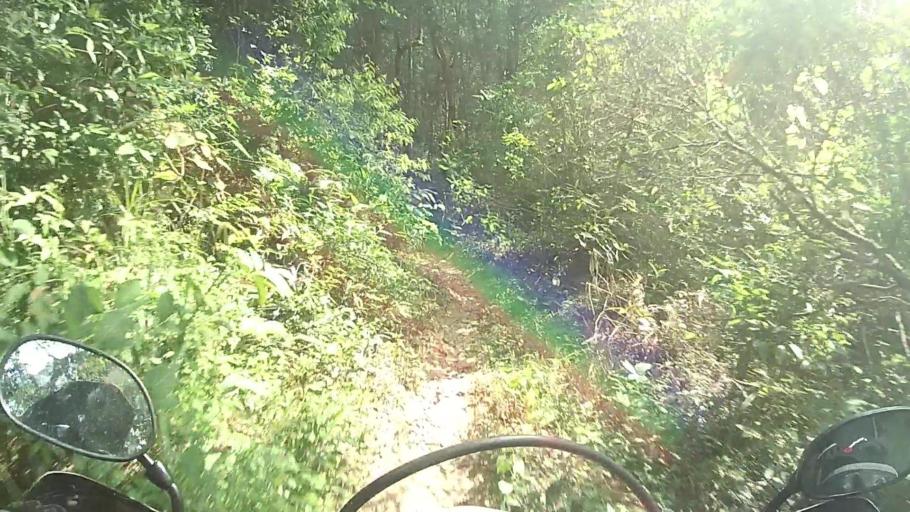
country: TH
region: Lampang
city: Mueang Pan
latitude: 18.7897
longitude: 99.3796
